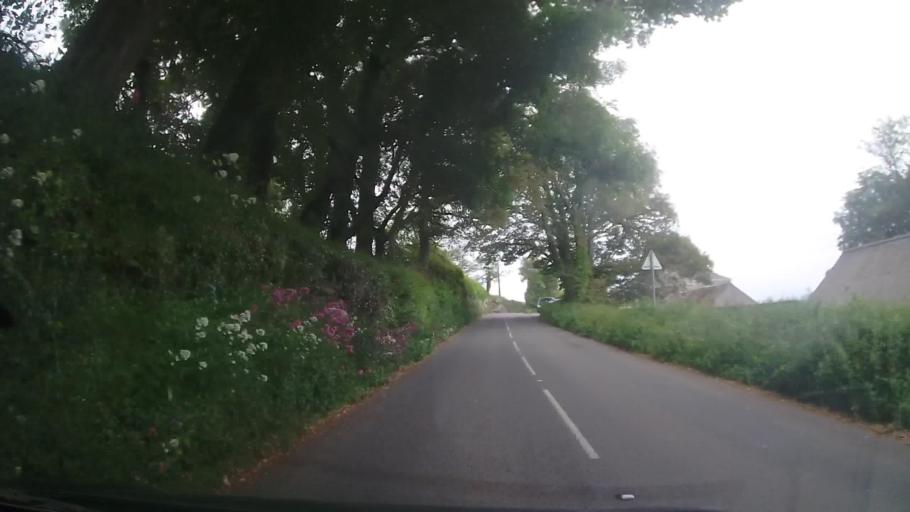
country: GB
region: England
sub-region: Devon
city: Dartmouth
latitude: 50.3152
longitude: -3.6261
